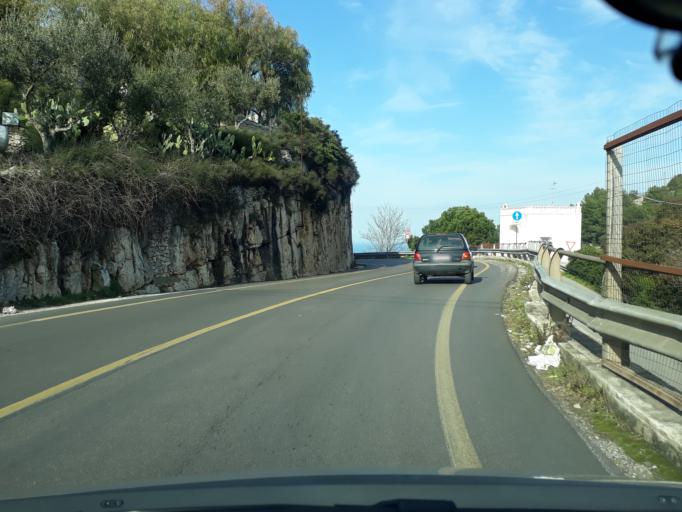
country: IT
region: Apulia
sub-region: Provincia di Brindisi
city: Lamie di Olimpie-Selva
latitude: 40.8009
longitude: 17.3522
